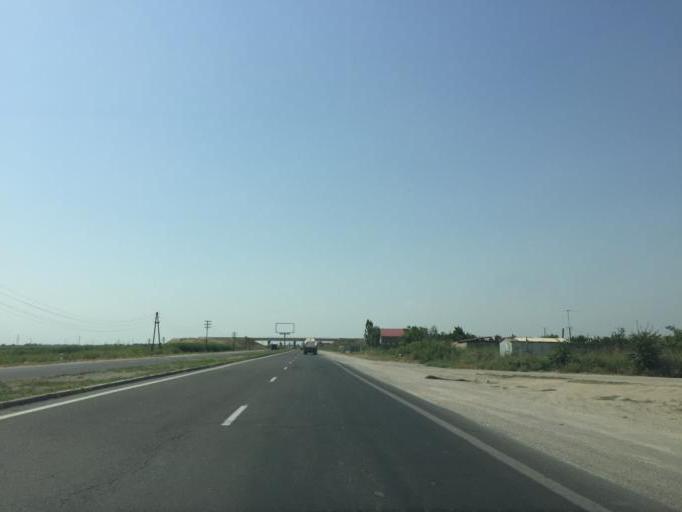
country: AM
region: Ararat
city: Shahumyan
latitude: 39.9298
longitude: 44.5712
